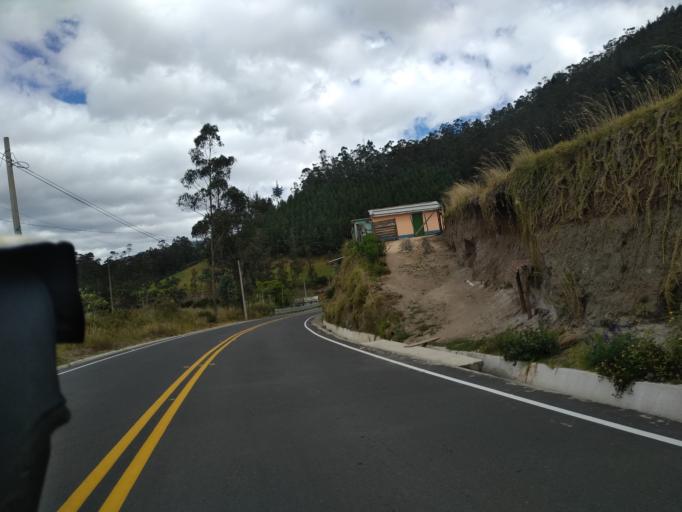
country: EC
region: Cotopaxi
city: Saquisili
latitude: -0.7146
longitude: -78.8851
